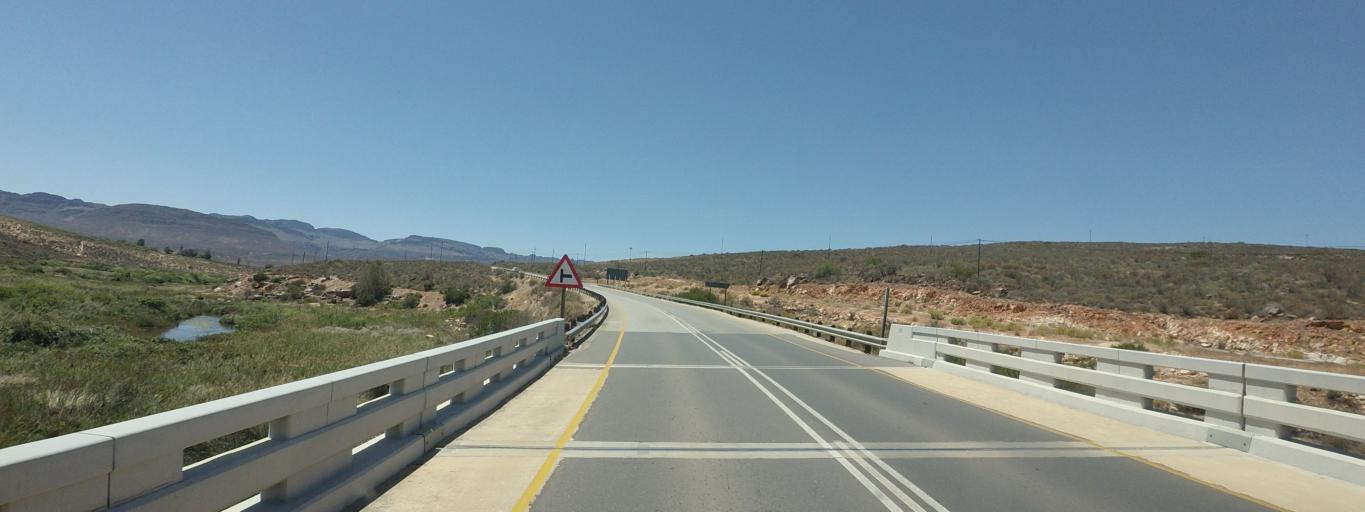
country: ZA
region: Western Cape
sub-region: West Coast District Municipality
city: Clanwilliam
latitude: -32.1729
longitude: 18.8708
